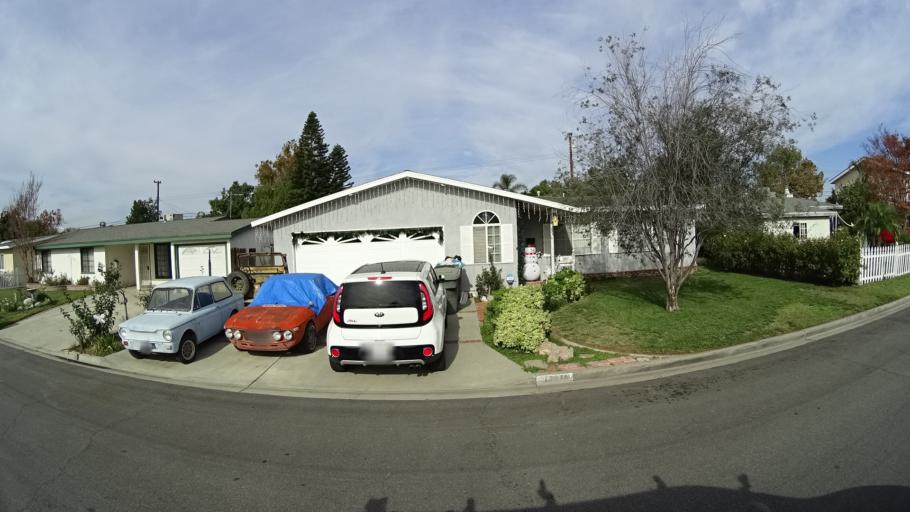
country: US
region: California
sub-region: Orange County
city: Garden Grove
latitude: 33.7825
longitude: -117.9121
